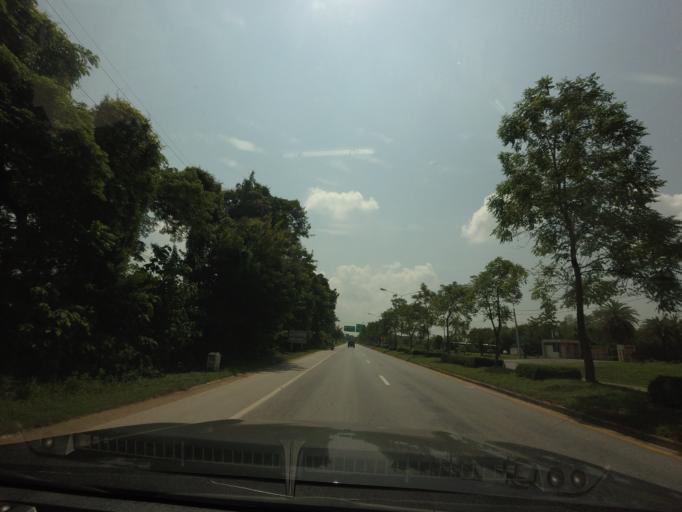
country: TH
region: Uttaradit
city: Uttaradit
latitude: 17.6128
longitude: 100.1236
